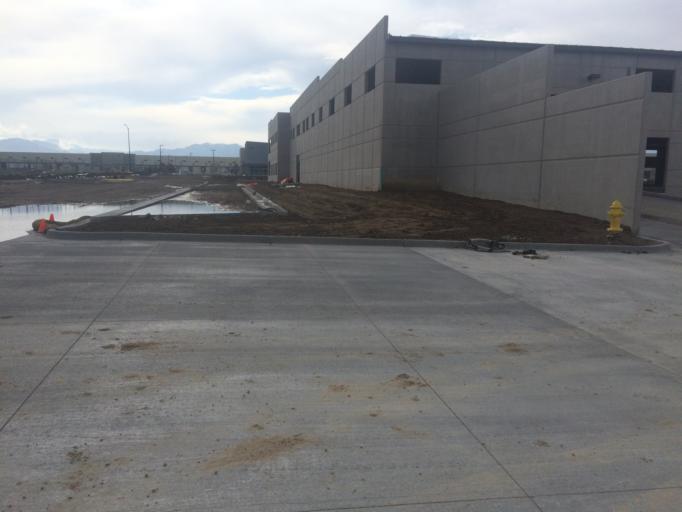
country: US
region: Colorado
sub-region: Boulder County
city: Louisville
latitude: 39.9601
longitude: -105.1112
